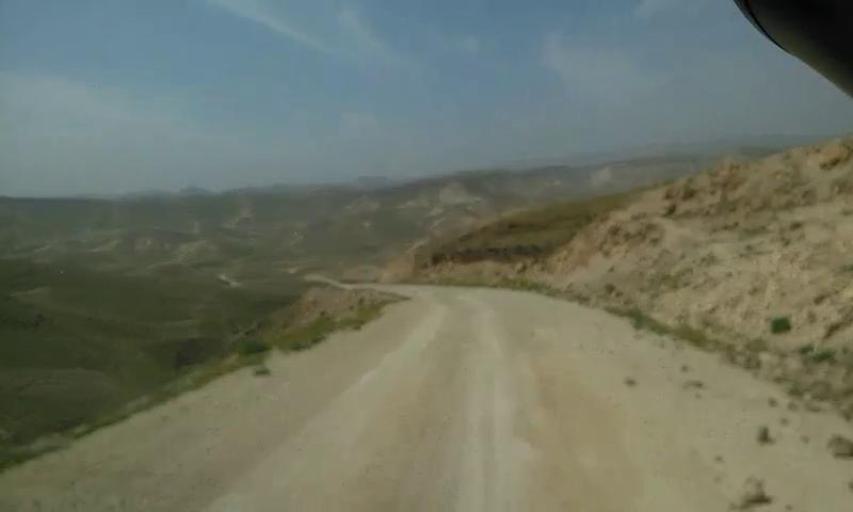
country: PS
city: `Arab ar Rashaydah
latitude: 31.5157
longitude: 35.2888
